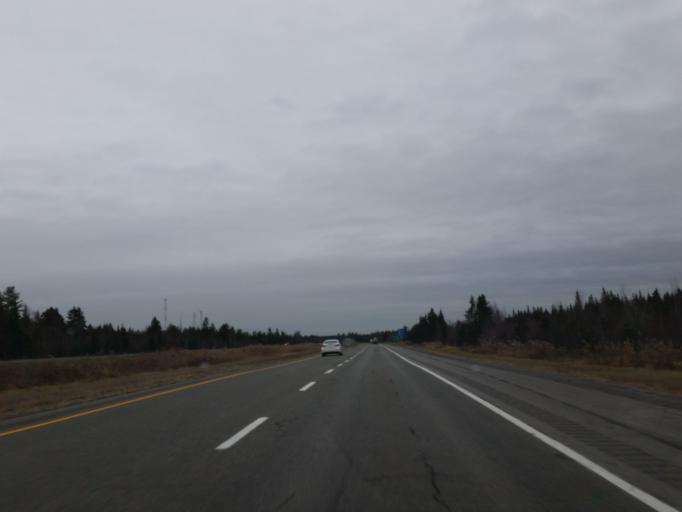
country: CA
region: Quebec
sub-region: Mauricie
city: Becancour
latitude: 46.4914
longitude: -72.3136
